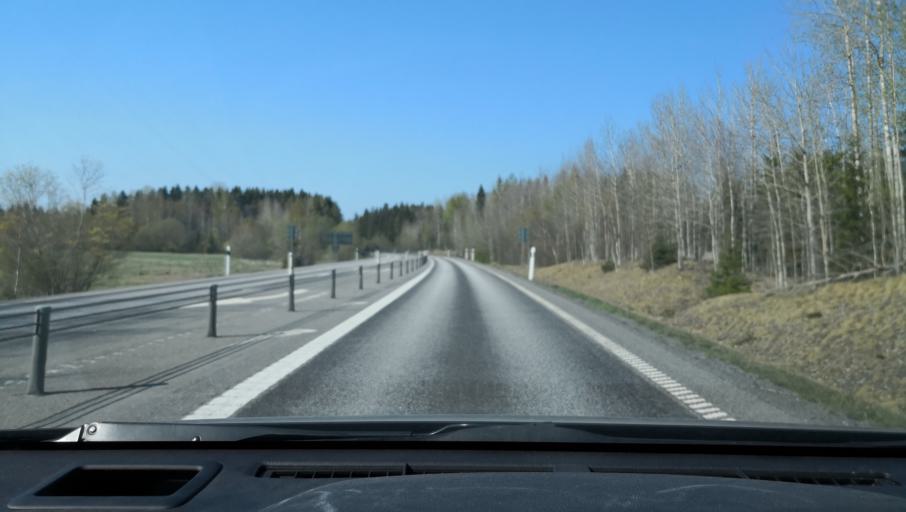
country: SE
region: Uppsala
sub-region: Heby Kommun
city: Tarnsjo
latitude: 60.1697
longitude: 16.9551
